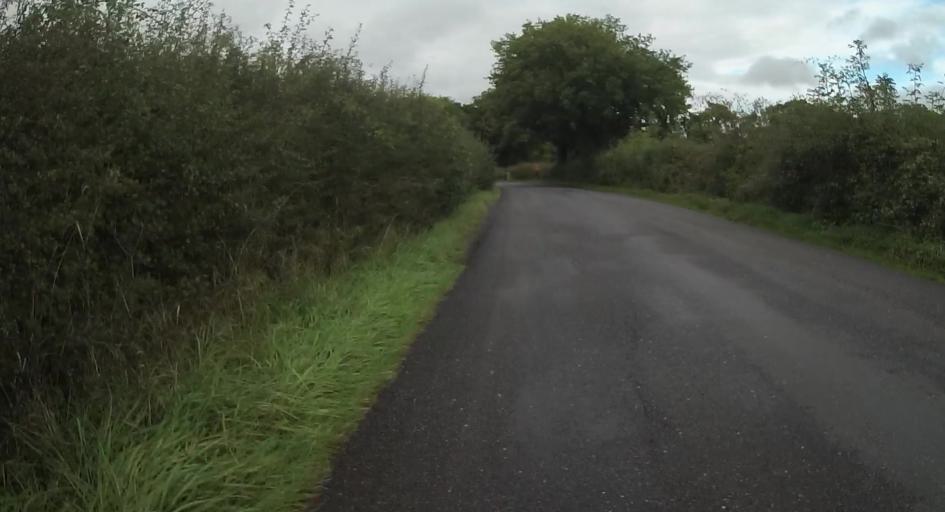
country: GB
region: England
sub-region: Hampshire
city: Tadley
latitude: 51.3056
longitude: -1.1529
